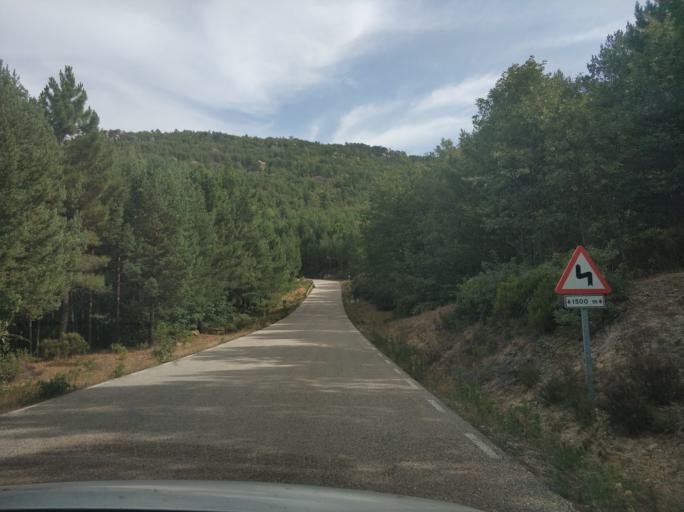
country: ES
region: Castille and Leon
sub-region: Provincia de Soria
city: Duruelo de la Sierra
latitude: 41.8994
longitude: -2.9404
